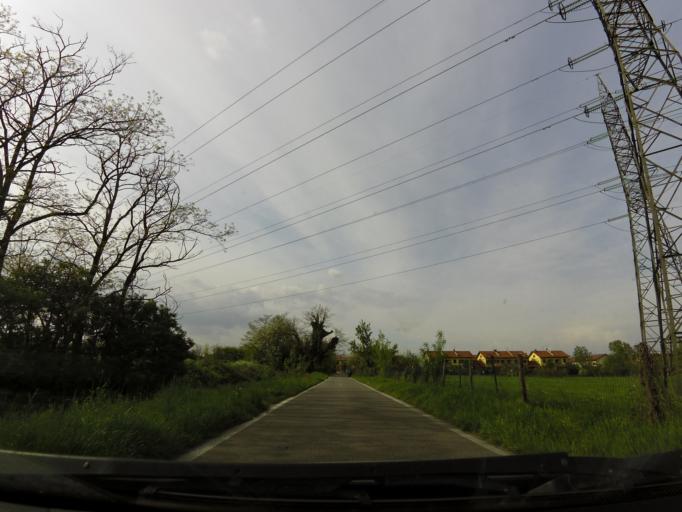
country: IT
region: Lombardy
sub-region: Citta metropolitana di Milano
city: Civesio
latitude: 45.3909
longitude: 9.2678
